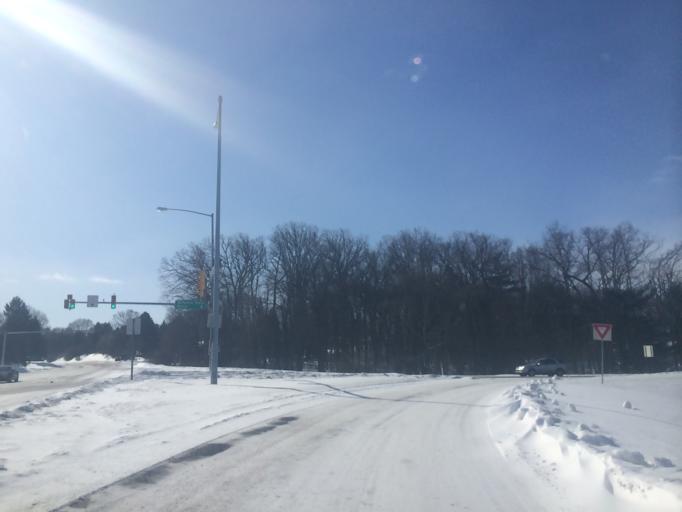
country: US
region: Pennsylvania
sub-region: Centre County
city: State College
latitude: 40.7738
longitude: -77.8874
